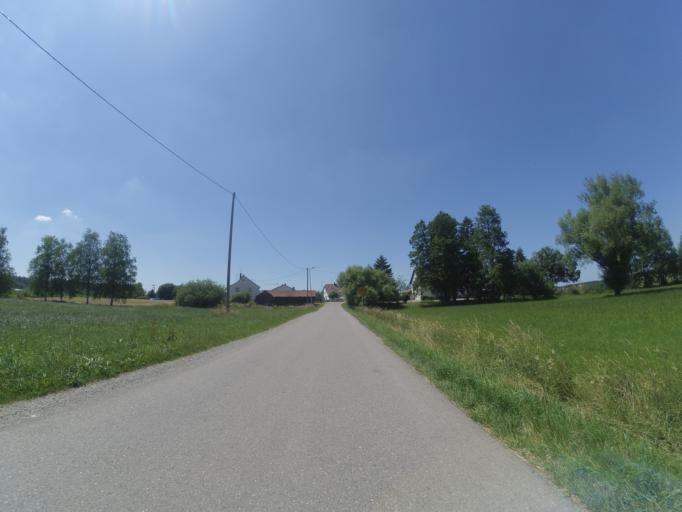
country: DE
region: Baden-Wuerttemberg
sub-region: Tuebingen Region
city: Bad Waldsee
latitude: 47.9232
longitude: 9.6978
